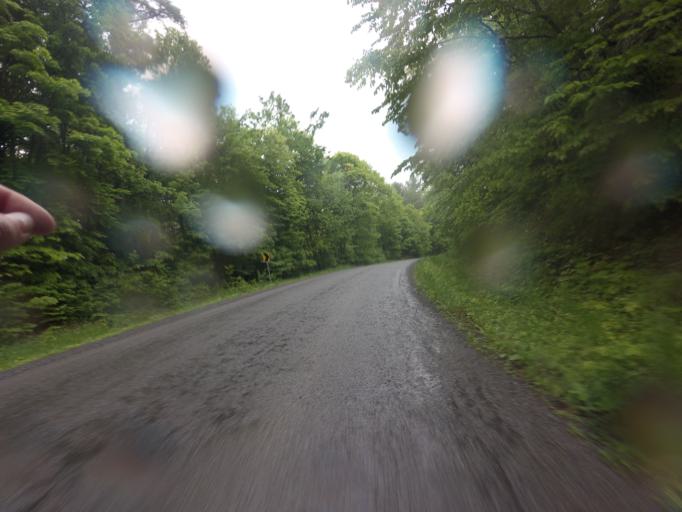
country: CA
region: Ontario
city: Gananoque
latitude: 44.5445
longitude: -76.3703
